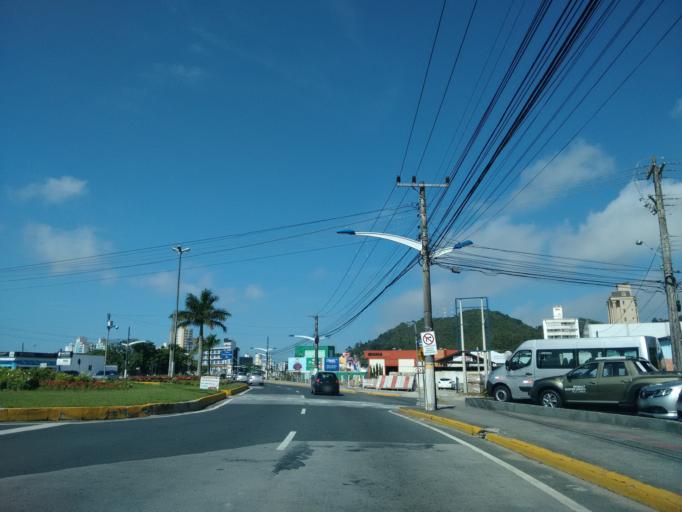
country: BR
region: Santa Catarina
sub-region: Itajai
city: Itajai
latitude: -26.9244
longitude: -48.6772
